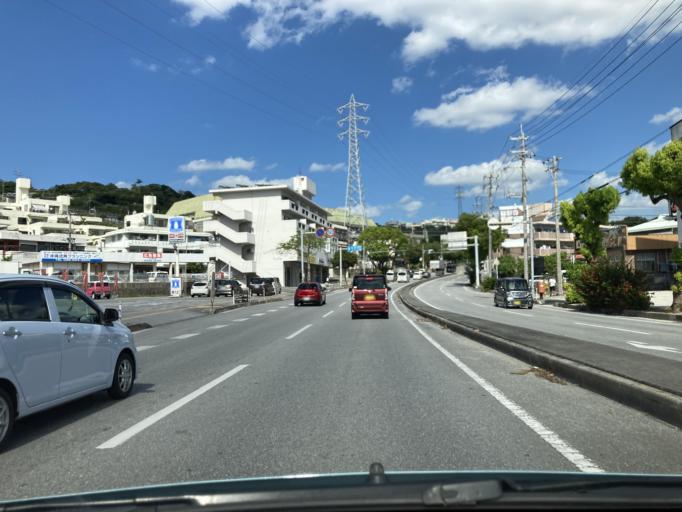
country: JP
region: Okinawa
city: Tomigusuku
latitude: 26.1998
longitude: 127.7143
